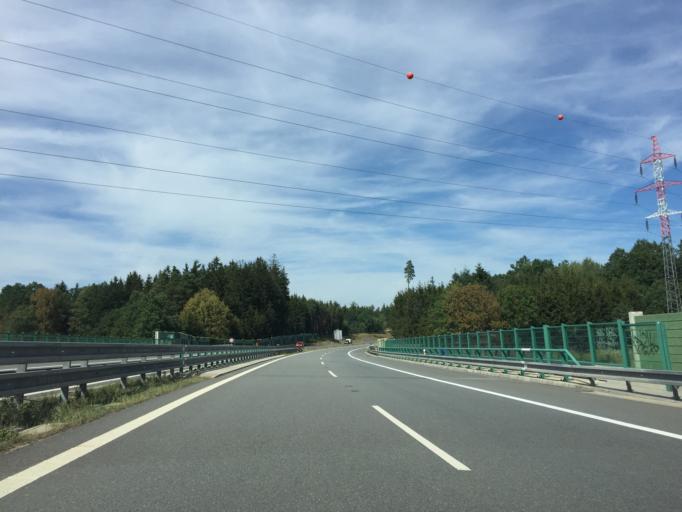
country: CZ
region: Jihocesky
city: Plana nad Luznici
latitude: 49.3729
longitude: 14.7202
